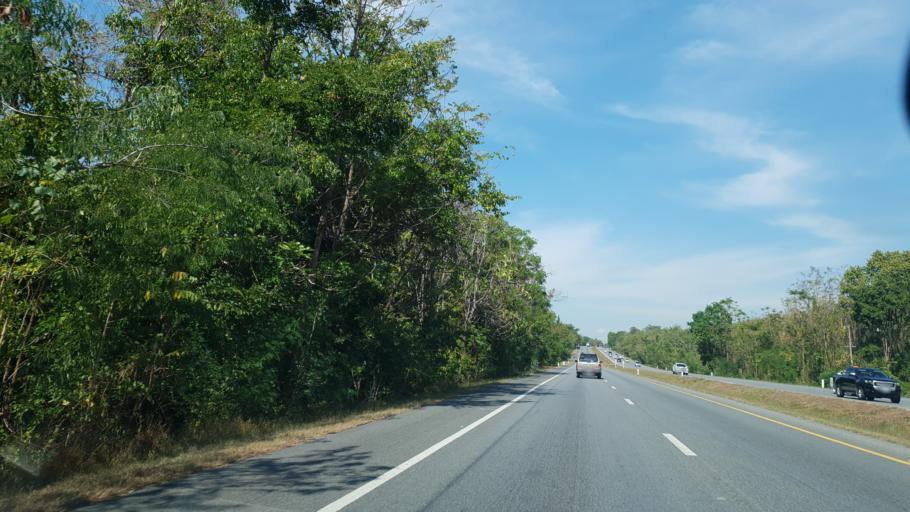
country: TH
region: Uttaradit
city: Thong Saen Khan
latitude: 17.4154
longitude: 100.2277
